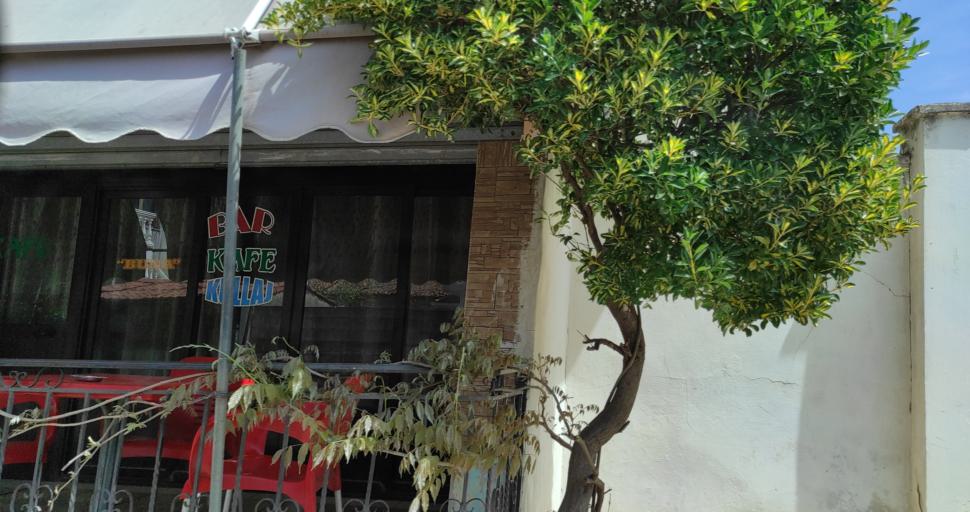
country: AL
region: Shkoder
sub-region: Rrethi i Malesia e Madhe
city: Gruemire
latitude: 42.1291
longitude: 19.5533
